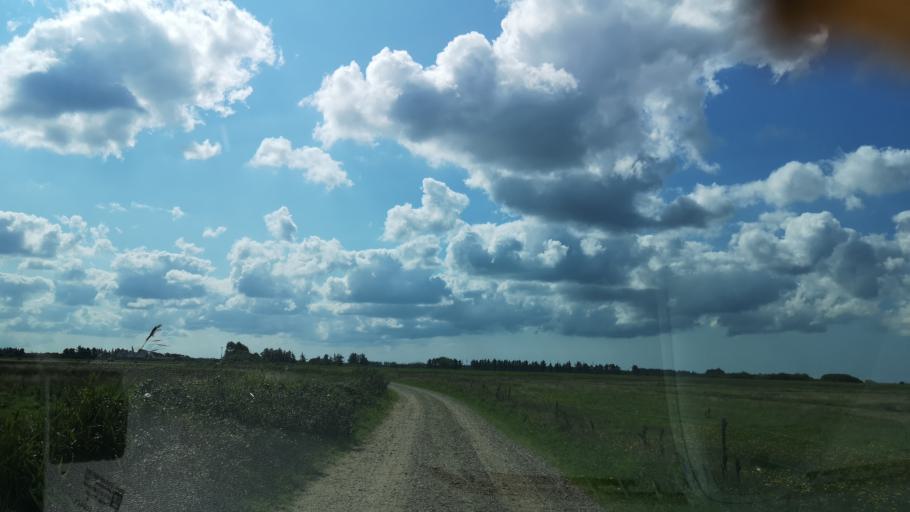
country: DK
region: Central Jutland
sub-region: Ringkobing-Skjern Kommune
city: Skjern
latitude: 55.9095
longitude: 8.4007
